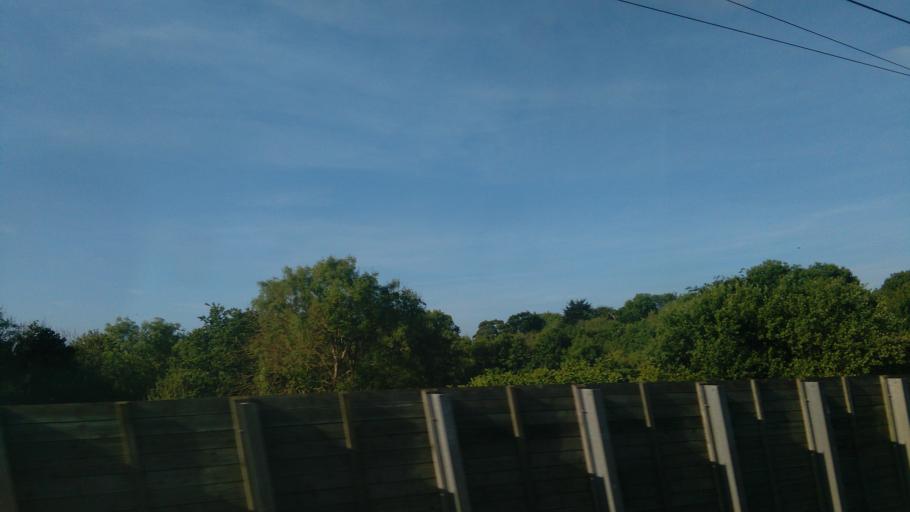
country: GB
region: England
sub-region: Kent
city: Hythe
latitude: 51.0910
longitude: 1.0665
